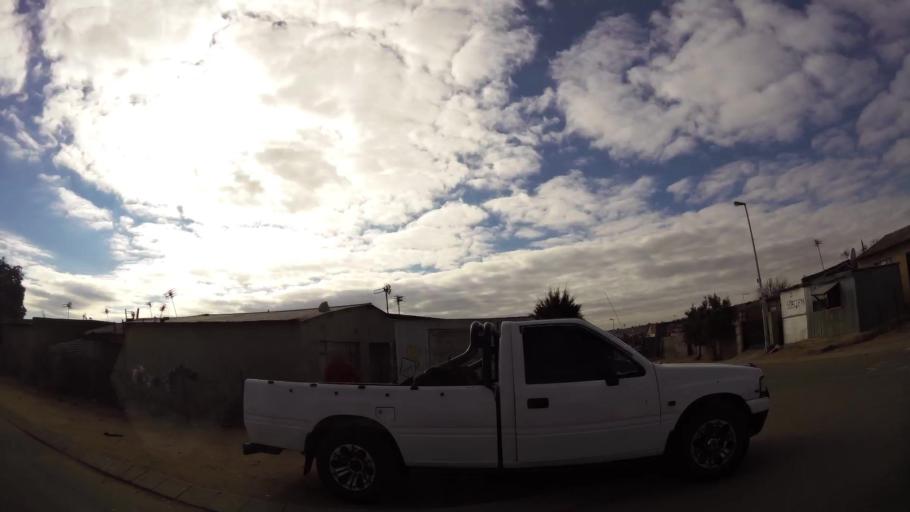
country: ZA
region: Gauteng
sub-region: City of Johannesburg Metropolitan Municipality
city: Modderfontein
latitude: -26.0423
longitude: 28.1834
